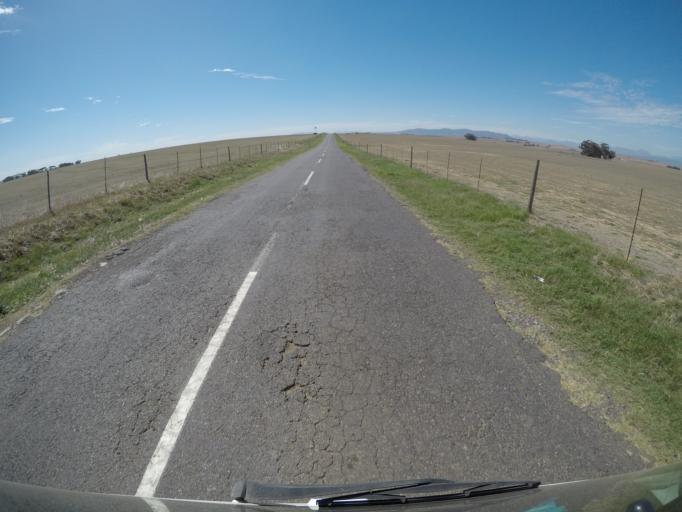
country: ZA
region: Western Cape
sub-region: City of Cape Town
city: Atlantis
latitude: -33.6885
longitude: 18.5965
